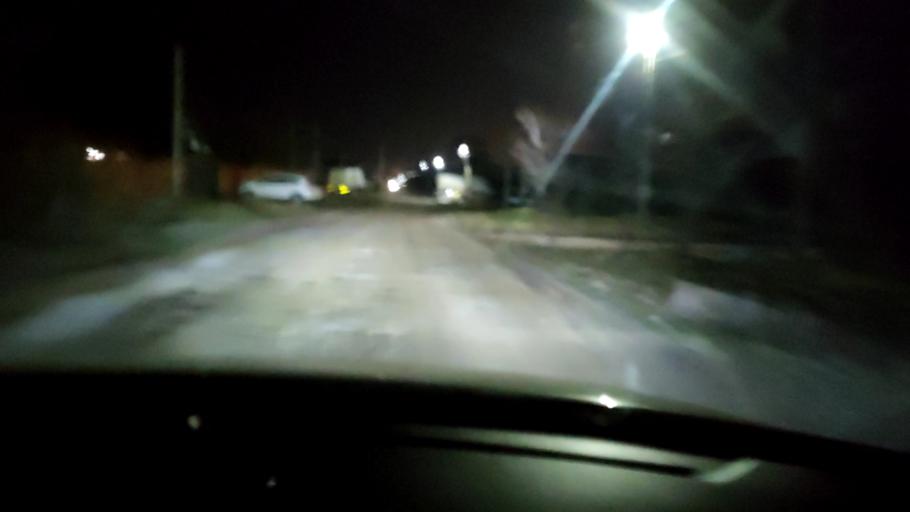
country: RU
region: Tatarstan
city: Stolbishchi
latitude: 55.7152
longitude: 49.3675
